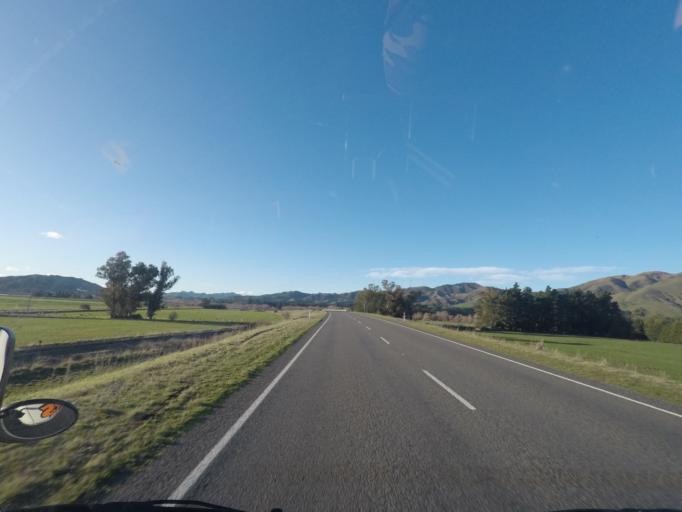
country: NZ
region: Canterbury
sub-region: Kaikoura District
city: Kaikoura
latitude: -42.7057
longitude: 173.2981
